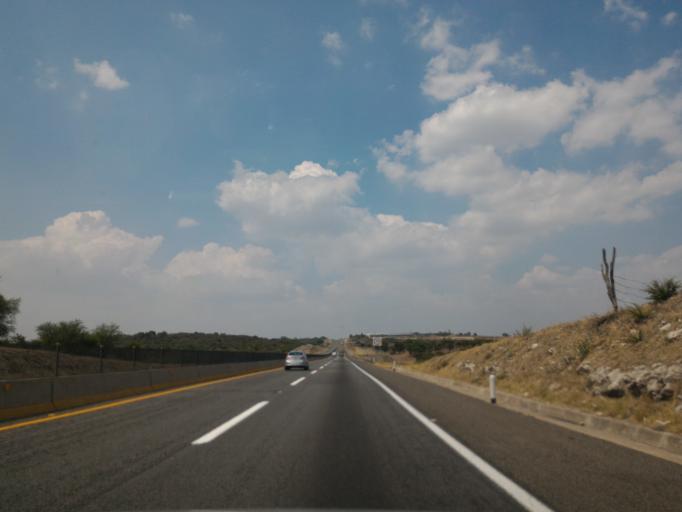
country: MX
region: Jalisco
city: San Juan de los Lagos
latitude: 21.2662
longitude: -102.2869
